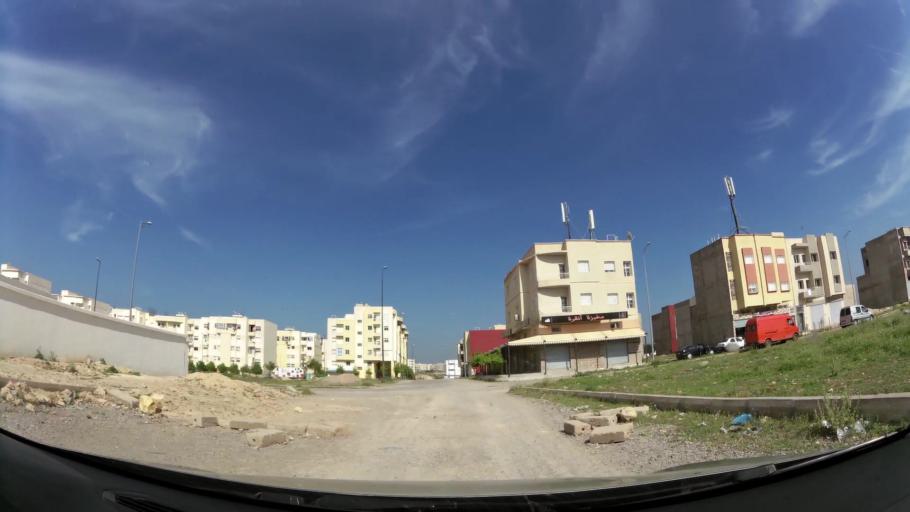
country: MA
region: Fes-Boulemane
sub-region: Fes
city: Fes
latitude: 34.0092
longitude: -5.0428
